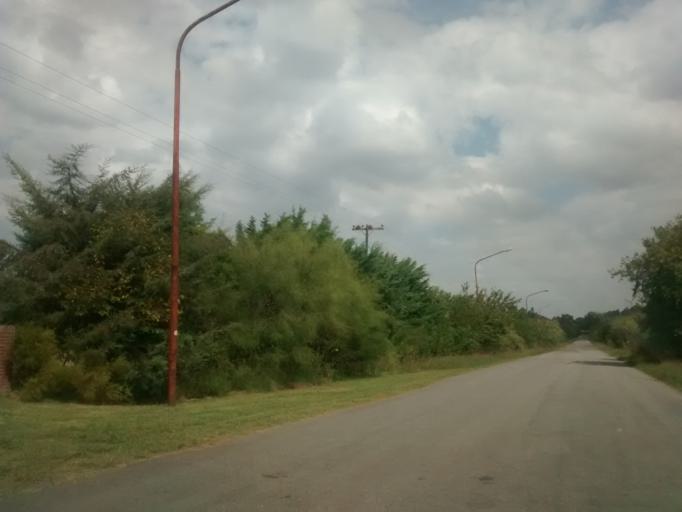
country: AR
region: Buenos Aires
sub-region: Partido de La Plata
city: La Plata
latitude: -35.0038
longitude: -57.9084
